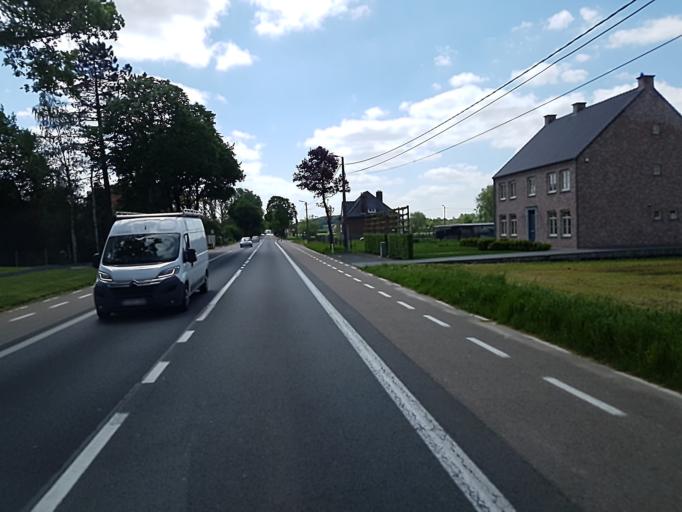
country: BE
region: Flanders
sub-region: Provincie Vlaams-Brabant
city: Glabbeek-Zuurbemde
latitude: 50.8609
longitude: 4.9552
